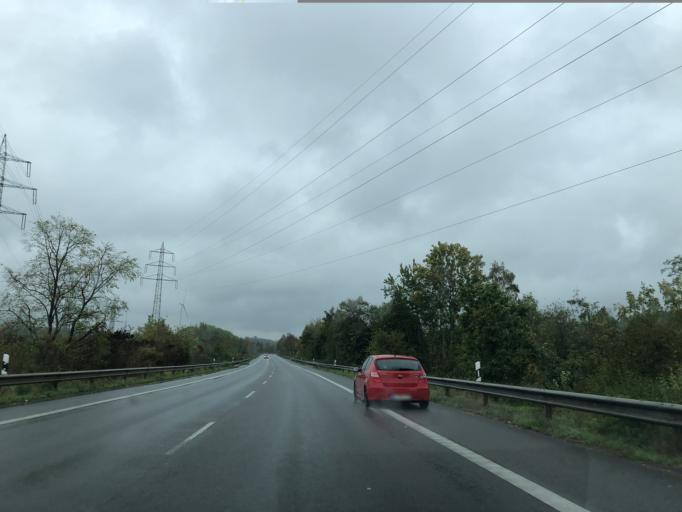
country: DE
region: North Rhine-Westphalia
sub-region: Regierungsbezirk Dusseldorf
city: Grevenbroich
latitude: 51.0541
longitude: 6.5633
